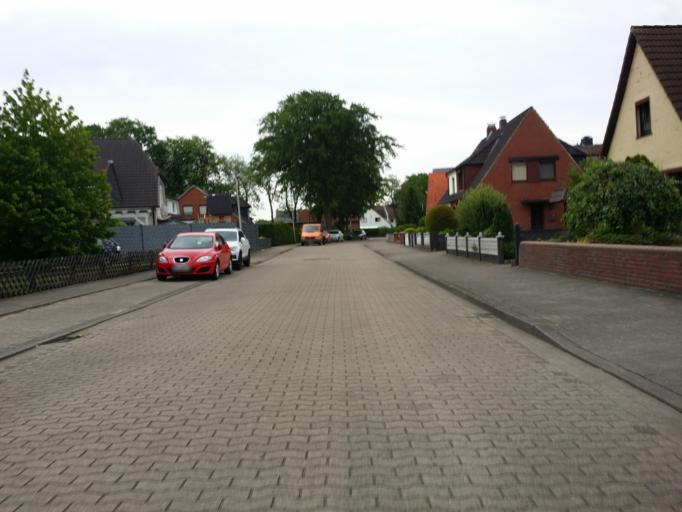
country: DE
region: Lower Saxony
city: Delmenhorst
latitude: 53.0454
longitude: 8.6490
